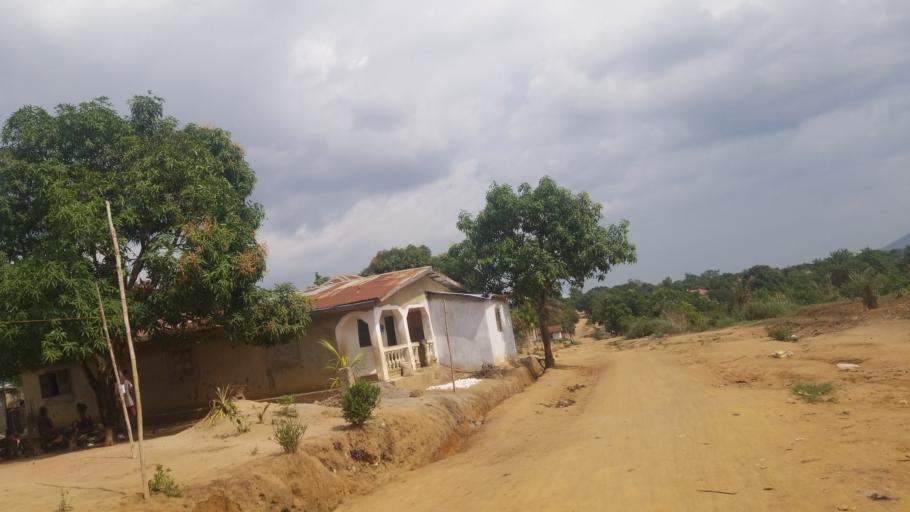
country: SL
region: Western Area
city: Waterloo
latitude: 8.3457
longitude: -13.0528
